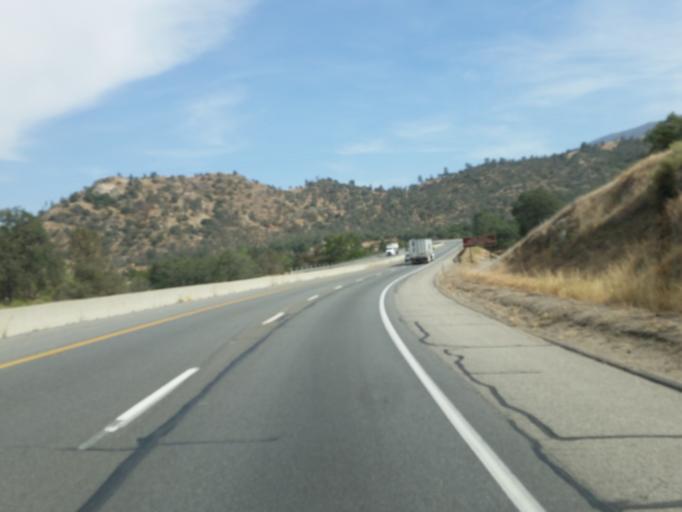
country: US
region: California
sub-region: Kern County
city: Bear Valley Springs
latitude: 35.2292
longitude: -118.5687
